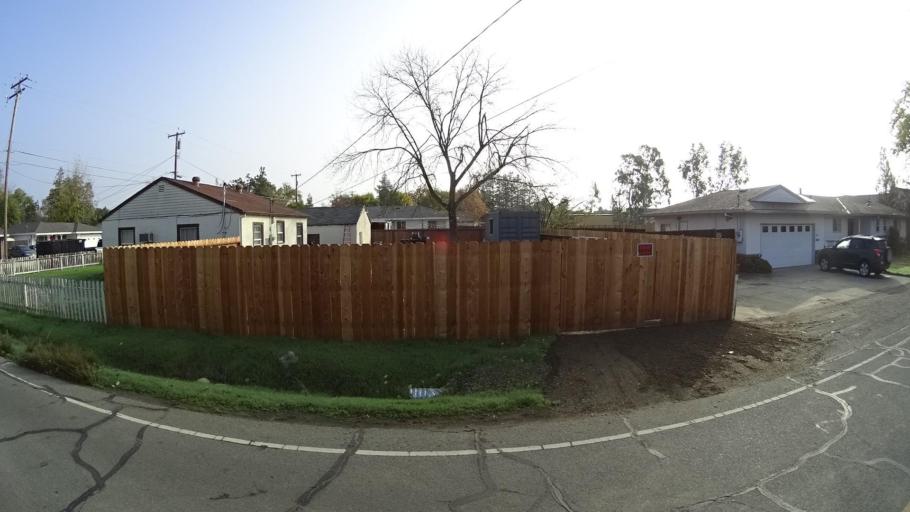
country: US
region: California
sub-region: Sacramento County
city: Elk Grove
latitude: 38.4052
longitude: -121.3596
